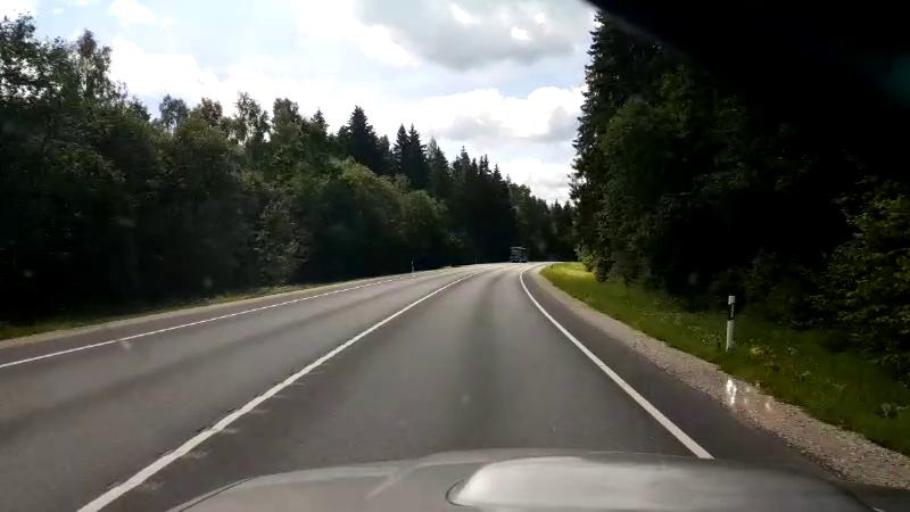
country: EE
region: Laeaene-Virumaa
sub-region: Tapa vald
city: Tapa
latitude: 59.2775
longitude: 26.0407
